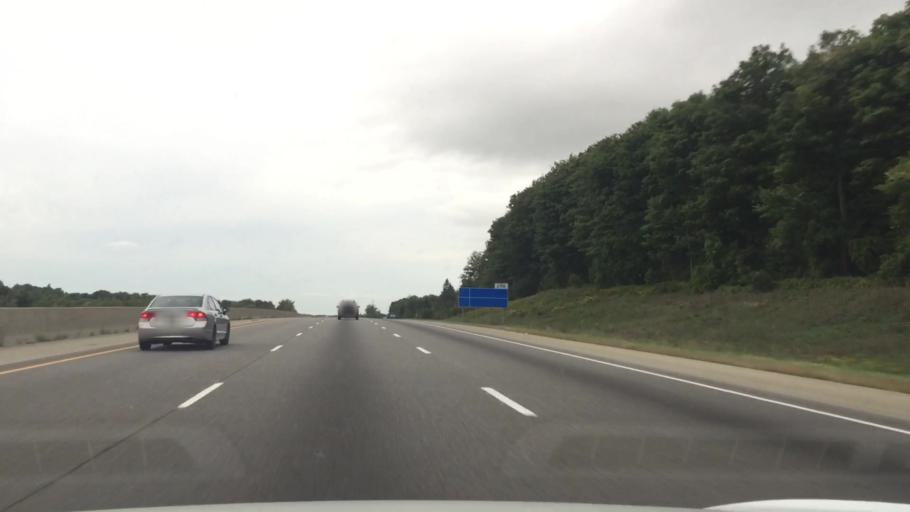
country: CA
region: Ontario
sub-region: Wellington County
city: Guelph
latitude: 43.4377
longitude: -80.2271
